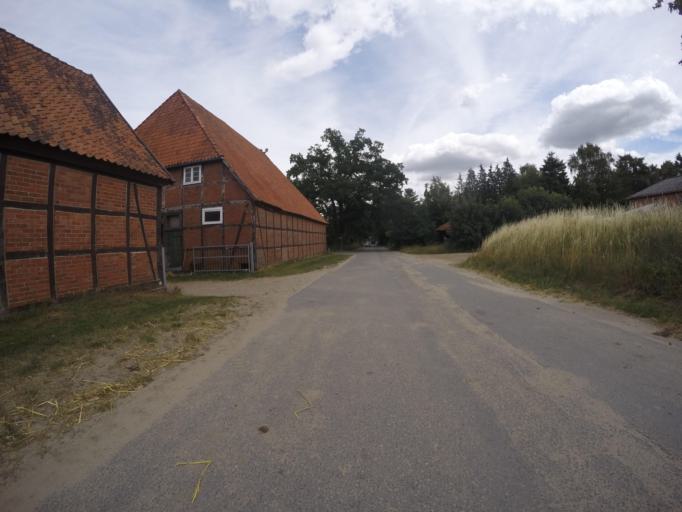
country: DE
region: Lower Saxony
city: Bleckede
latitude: 53.2632
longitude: 10.7052
